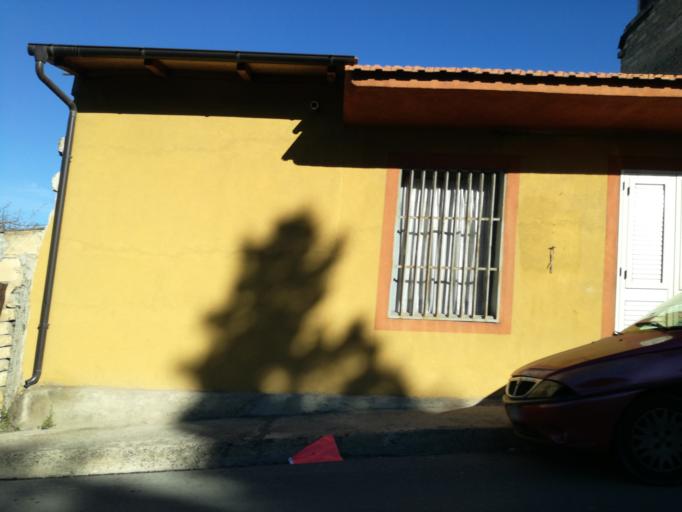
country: IT
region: Sicily
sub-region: Provincia di Caltanissetta
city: Gela
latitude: 37.0732
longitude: 14.2236
